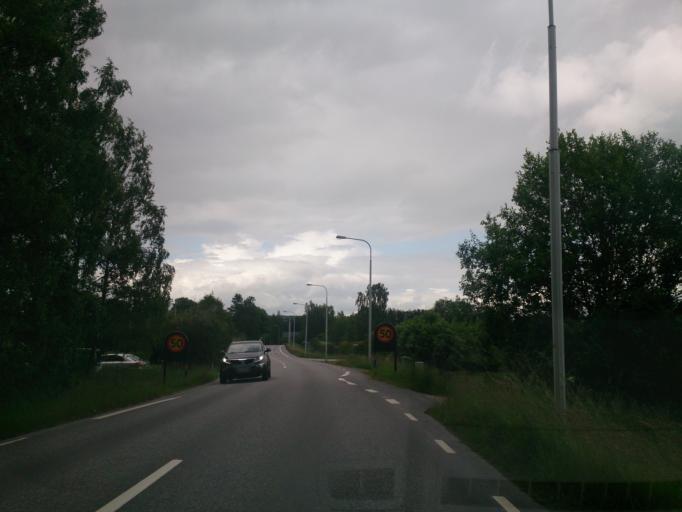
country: SE
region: OEstergoetland
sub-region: Norrkopings Kommun
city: Norrkoping
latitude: 58.4832
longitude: 16.1719
